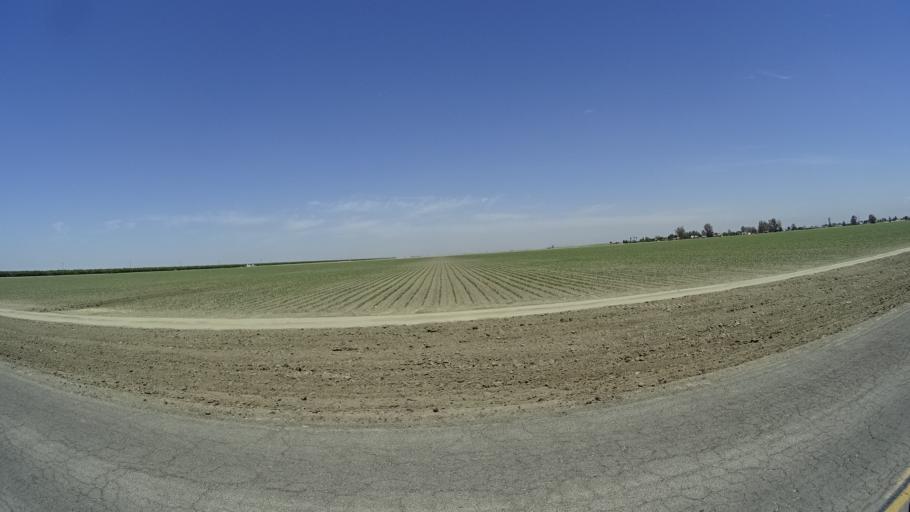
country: US
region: California
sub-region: Kings County
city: Corcoran
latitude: 36.1090
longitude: -119.5862
